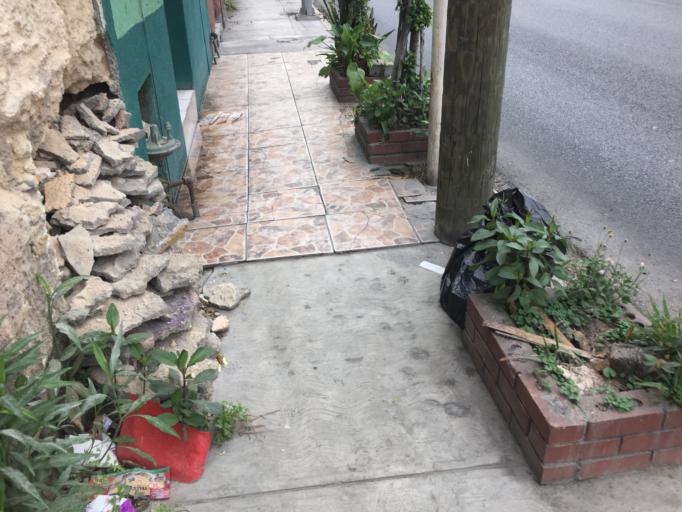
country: MX
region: Nuevo Leon
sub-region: Monterrey
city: Monterrey
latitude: 25.6787
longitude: -100.3059
